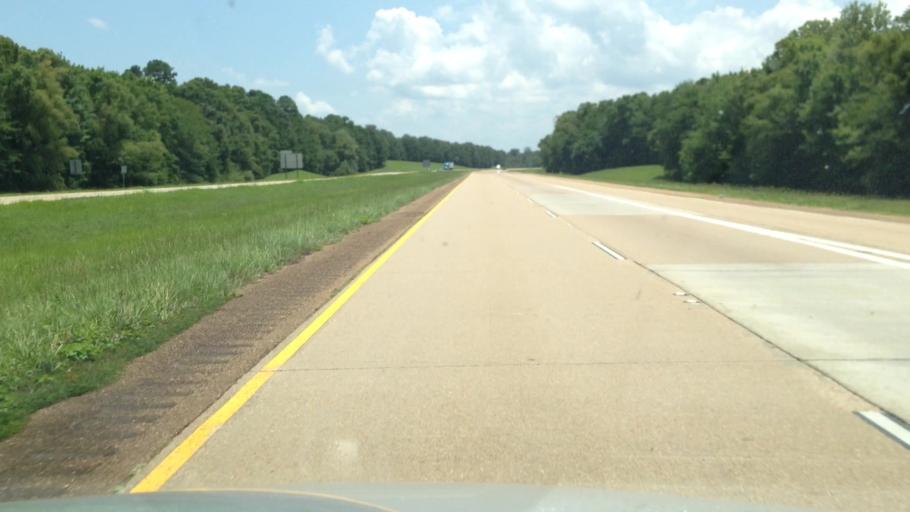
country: US
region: Louisiana
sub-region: Rapides Parish
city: Woodworth
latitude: 31.1595
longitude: -92.4571
